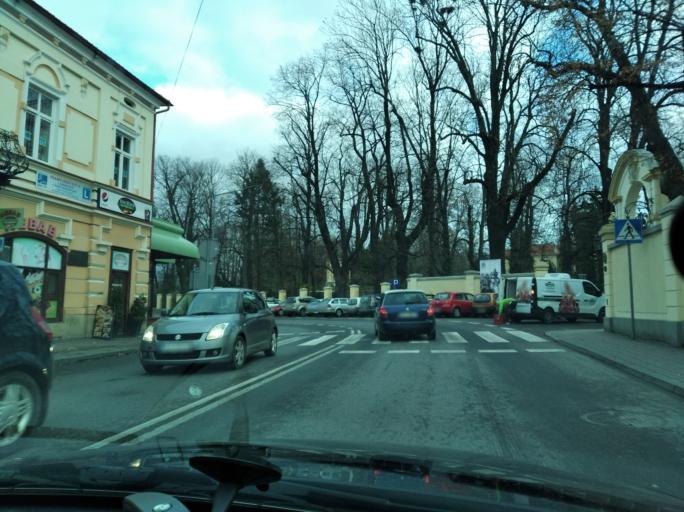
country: PL
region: Subcarpathian Voivodeship
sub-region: Powiat lancucki
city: Lancut
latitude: 50.0687
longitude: 22.2317
